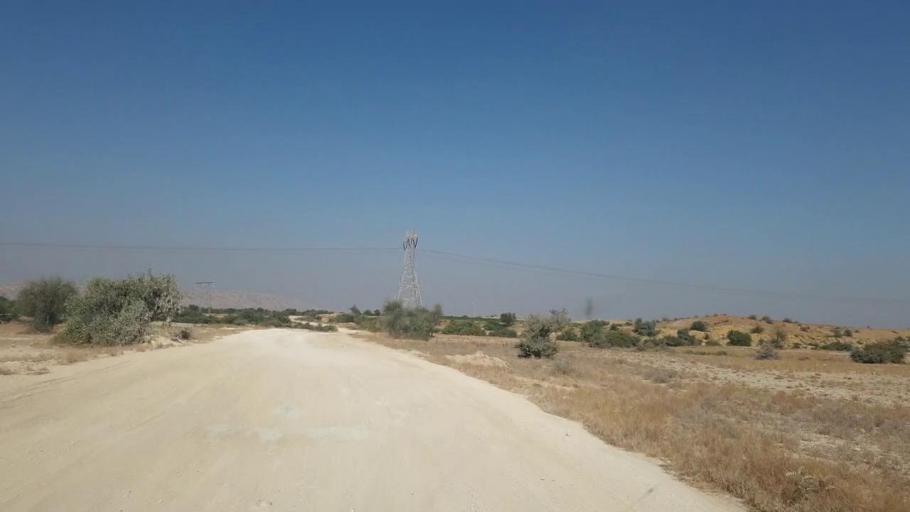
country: PK
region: Sindh
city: Thatta
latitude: 25.2429
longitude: 67.8046
